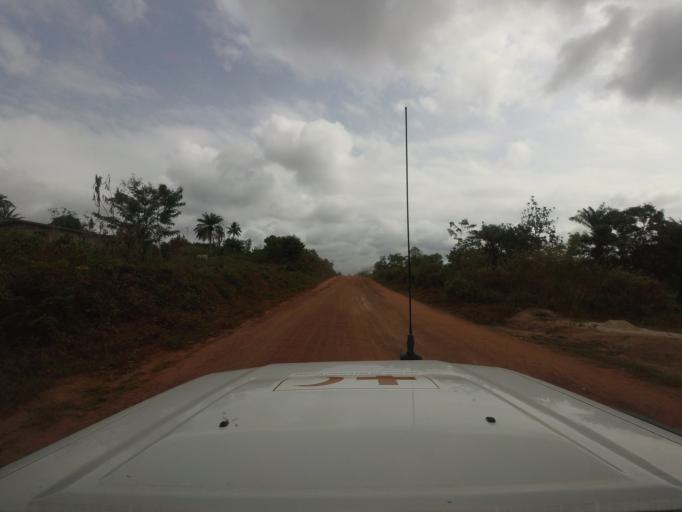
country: LR
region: Bong
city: Gbarnga
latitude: 7.0217
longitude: -9.4721
